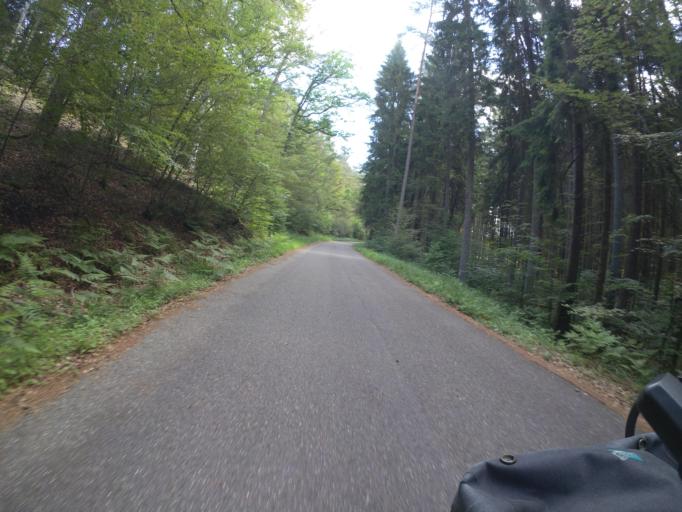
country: DE
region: Rheinland-Pfalz
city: Dahn
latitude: 49.1490
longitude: 7.7242
